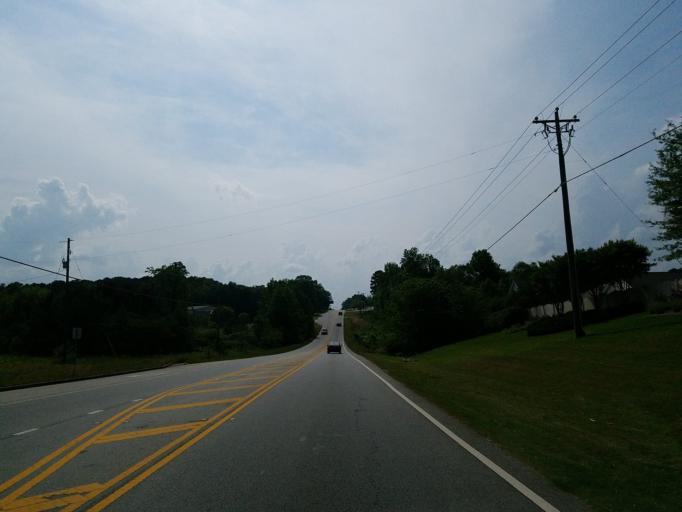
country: US
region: Georgia
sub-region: Paulding County
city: Hiram
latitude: 33.9100
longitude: -84.7854
